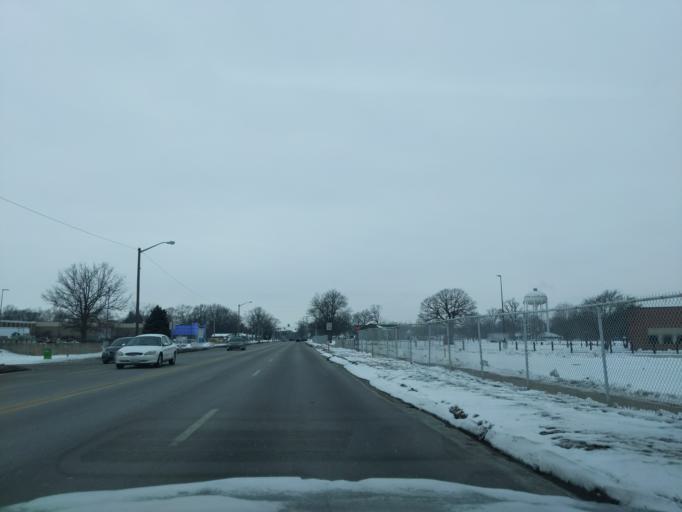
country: US
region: Indiana
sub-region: Tippecanoe County
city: Lafayette
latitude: 40.3955
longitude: -86.8732
